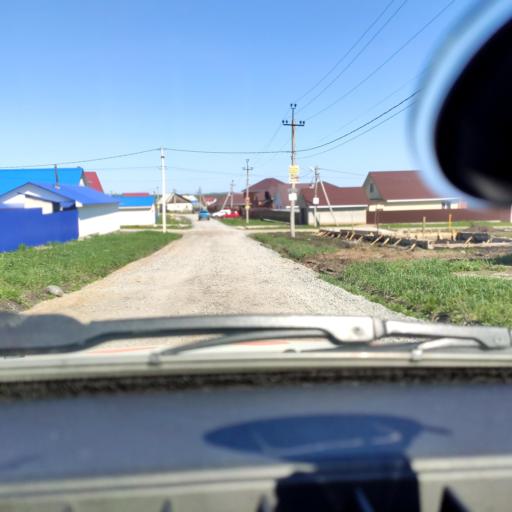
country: RU
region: Bashkortostan
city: Iglino
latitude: 54.7939
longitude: 56.2790
